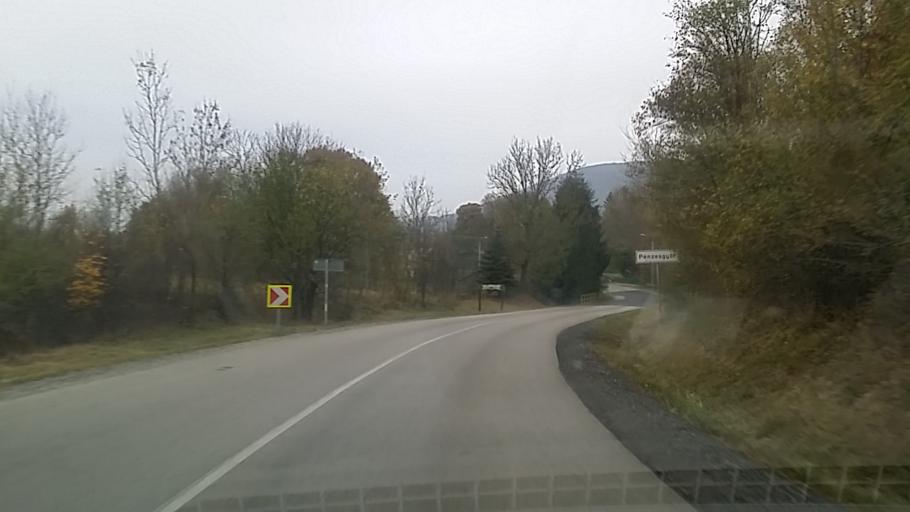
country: HU
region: Veszprem
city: Zirc
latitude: 47.2282
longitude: 17.7968
